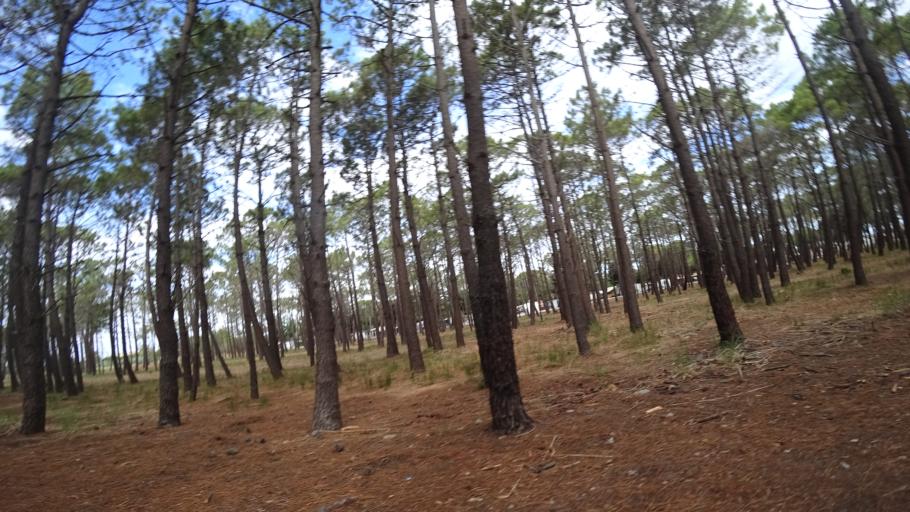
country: FR
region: Languedoc-Roussillon
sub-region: Departement des Pyrenees-Orientales
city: Le Barcares
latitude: 42.8203
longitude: 3.0343
